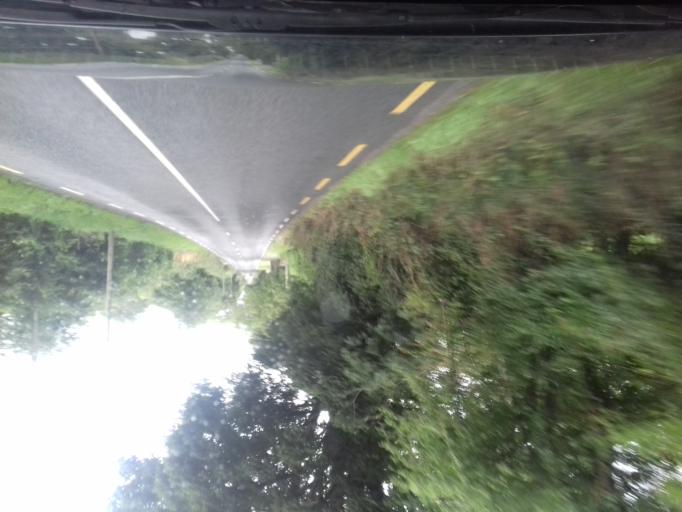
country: IE
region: Leinster
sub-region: Kilkenny
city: Graiguenamanagh
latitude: 52.6197
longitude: -6.9388
